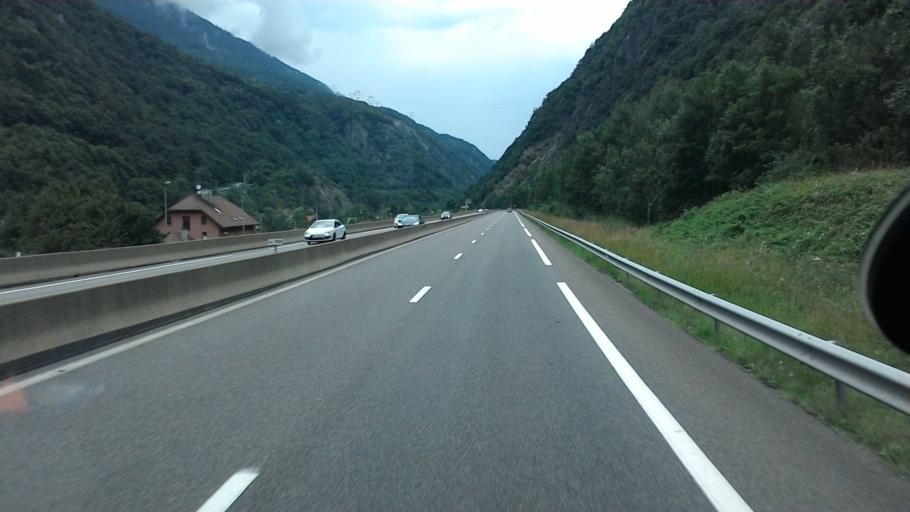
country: FR
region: Rhone-Alpes
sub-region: Departement de la Savoie
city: Aigueblanche
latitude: 45.5381
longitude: 6.4702
